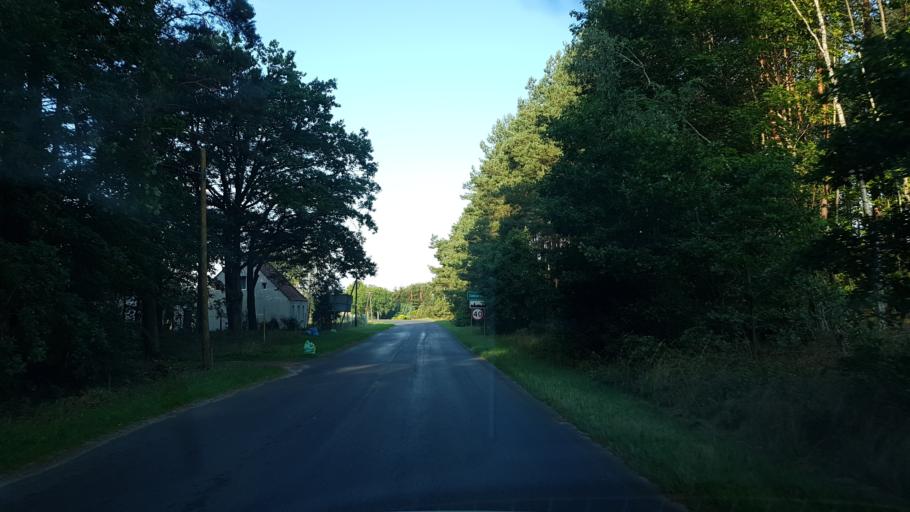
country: PL
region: West Pomeranian Voivodeship
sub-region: Powiat goleniowski
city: Przybiernow
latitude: 53.7606
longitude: 14.7551
